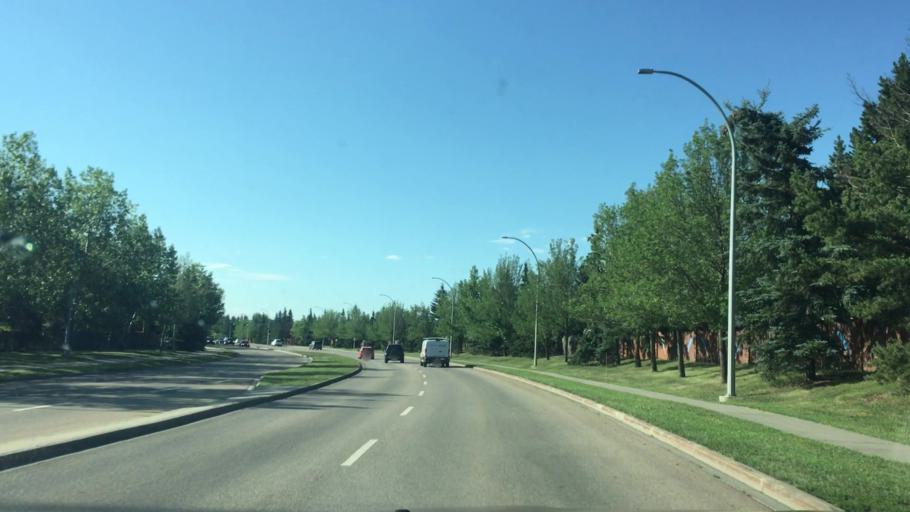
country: CA
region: Alberta
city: Edmonton
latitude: 53.4614
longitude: -113.5389
